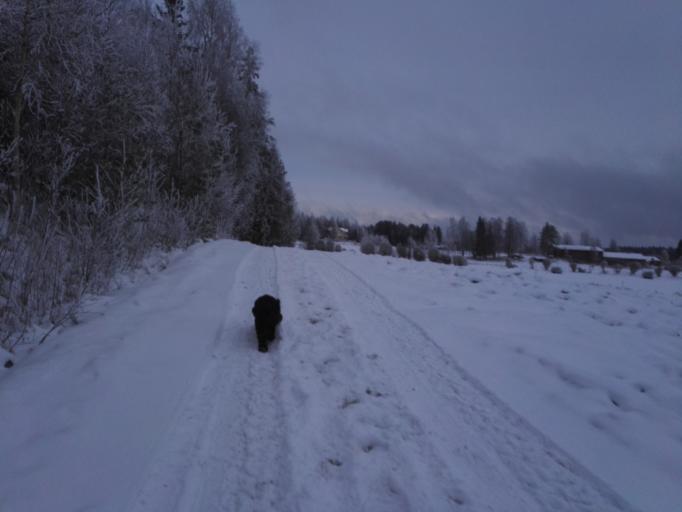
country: FI
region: Satakunta
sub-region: Pohjois-Satakunta
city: Jaemijaervi
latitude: 61.7844
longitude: 22.8742
